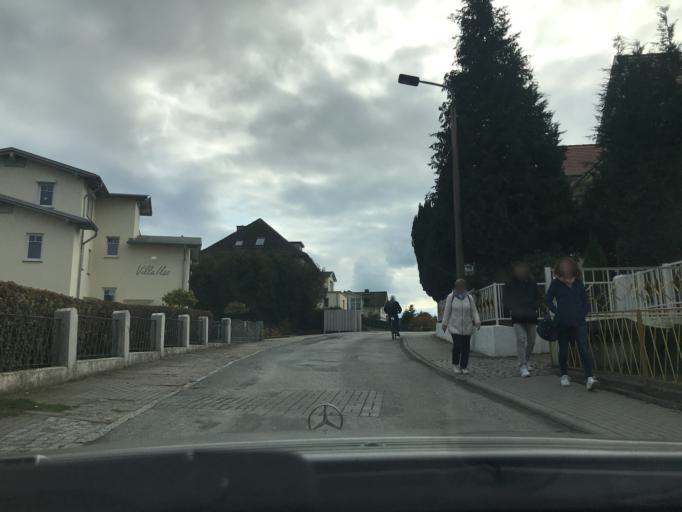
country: DE
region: Mecklenburg-Vorpommern
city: Seebad Heringsdorf
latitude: 53.9590
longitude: 14.1569
